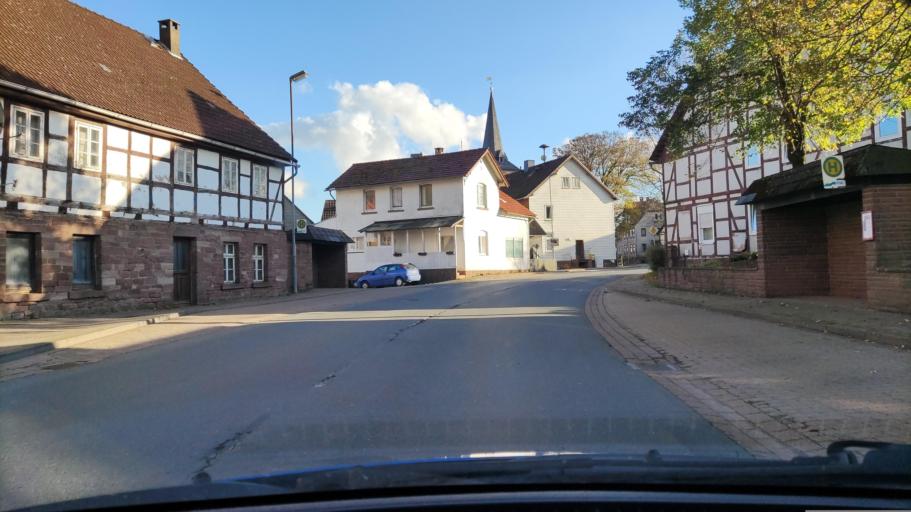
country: DE
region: Lower Saxony
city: Heinade
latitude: 51.8396
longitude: 9.6326
